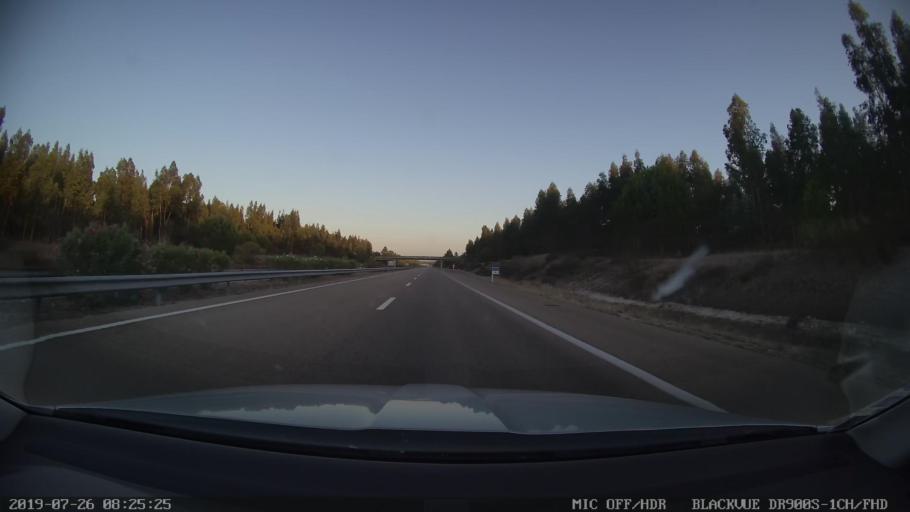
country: PT
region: Evora
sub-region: Vendas Novas
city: Vendas Novas
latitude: 38.6342
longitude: -8.6625
